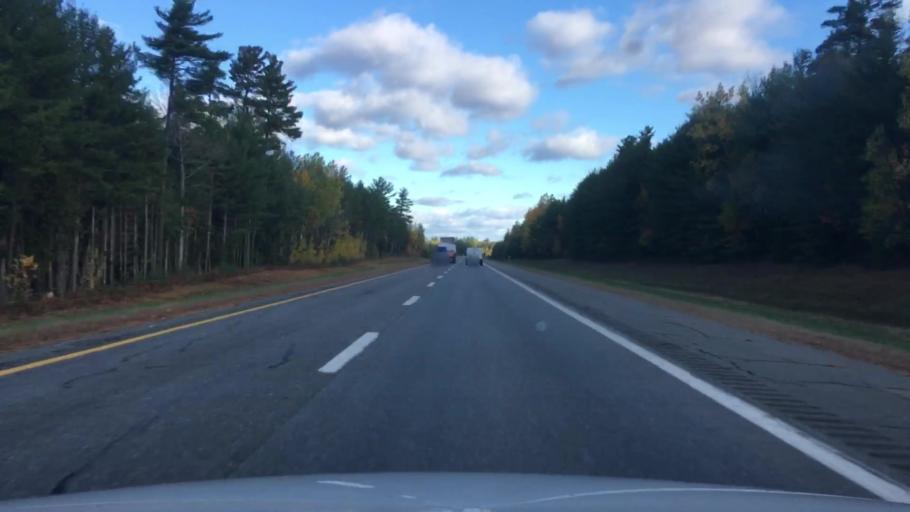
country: US
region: Maine
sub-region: Penobscot County
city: Greenbush
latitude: 45.1412
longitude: -68.7006
